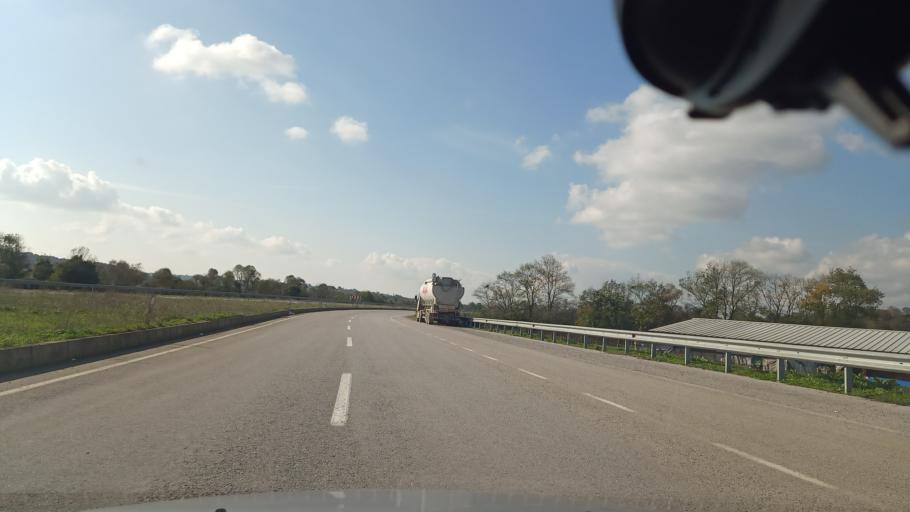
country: TR
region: Sakarya
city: Kaynarca
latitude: 41.0739
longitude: 30.3994
